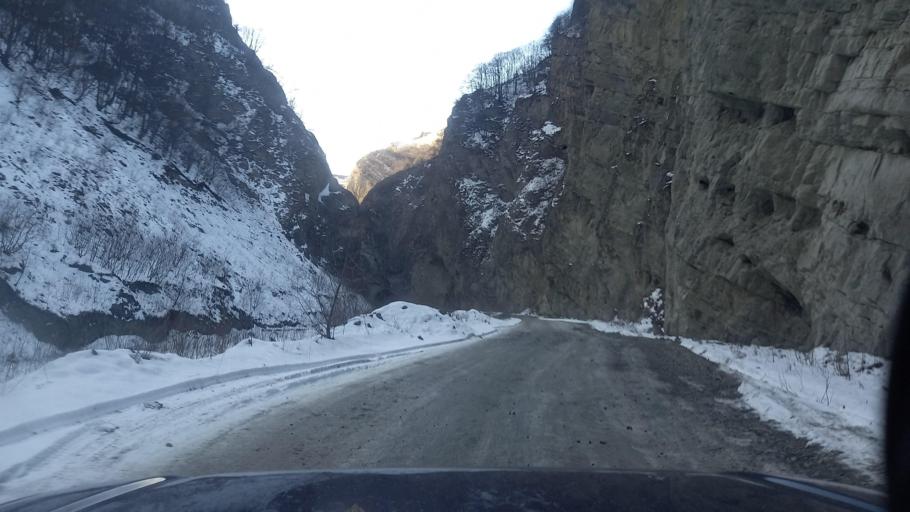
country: RU
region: Ingushetiya
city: Dzhayrakh
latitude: 42.8736
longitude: 44.5228
